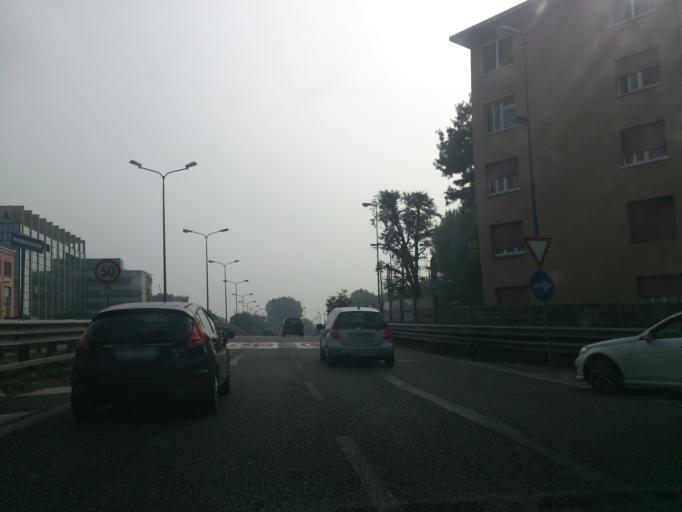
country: IT
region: Lombardy
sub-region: Citta metropolitana di Milano
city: Chiaravalle
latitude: 45.4373
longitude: 9.2295
